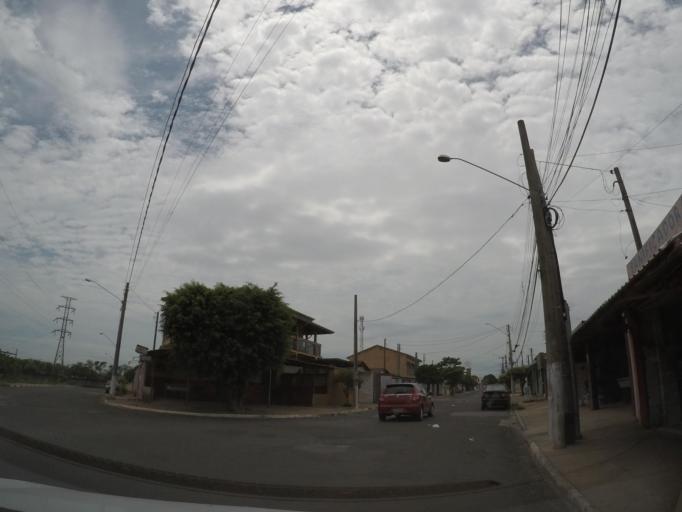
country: BR
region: Sao Paulo
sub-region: Hortolandia
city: Hortolandia
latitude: -22.8359
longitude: -47.2002
